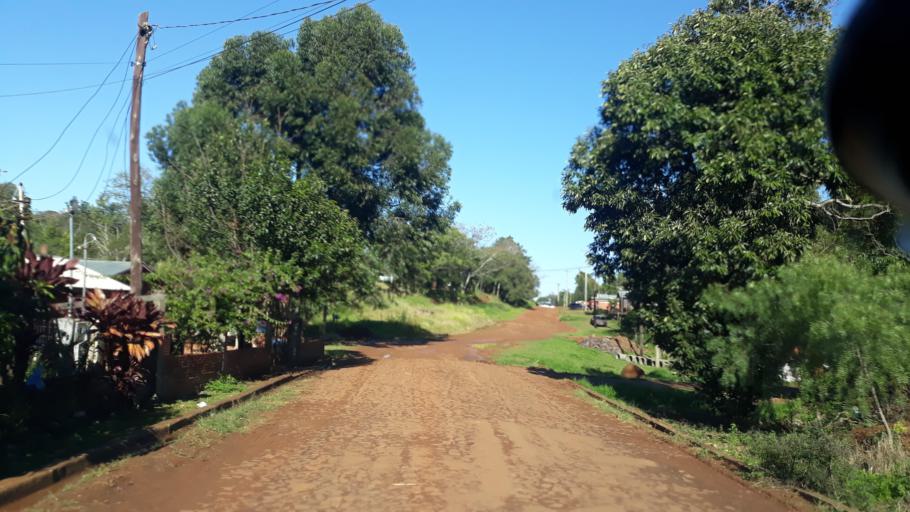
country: AR
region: Misiones
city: Bernardo de Irigoyen
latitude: -26.2633
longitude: -53.6576
